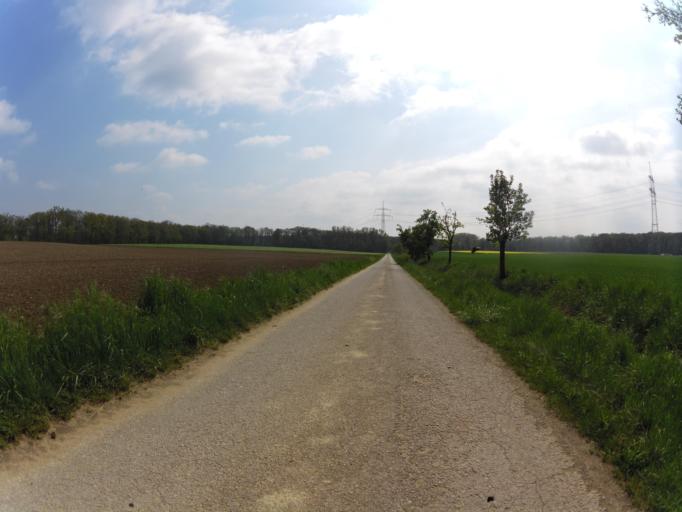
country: DE
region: Bavaria
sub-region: Regierungsbezirk Unterfranken
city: Sommerhausen
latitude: 49.7088
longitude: 10.0689
